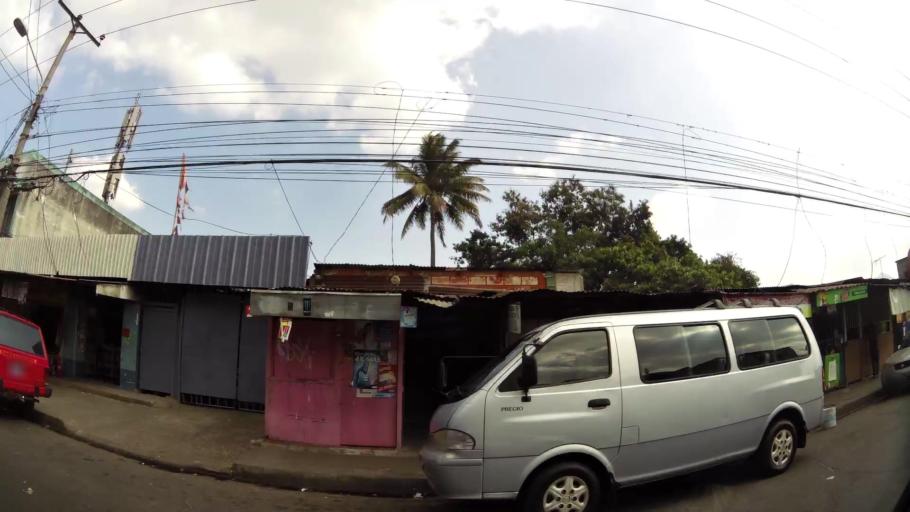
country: SV
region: San Salvador
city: Delgado
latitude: 13.7207
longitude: -89.1693
